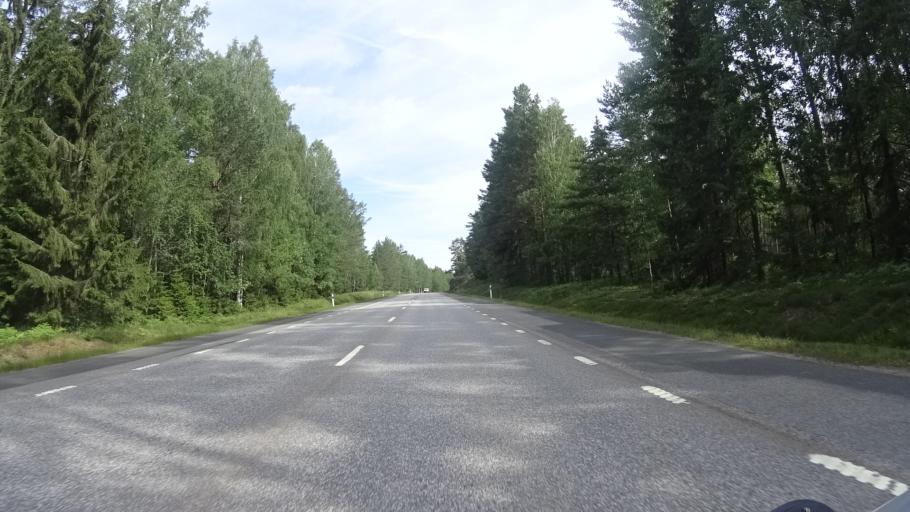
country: SE
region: Kalmar
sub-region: Vasterviks Kommun
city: Ankarsrum
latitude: 57.6872
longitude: 16.4409
